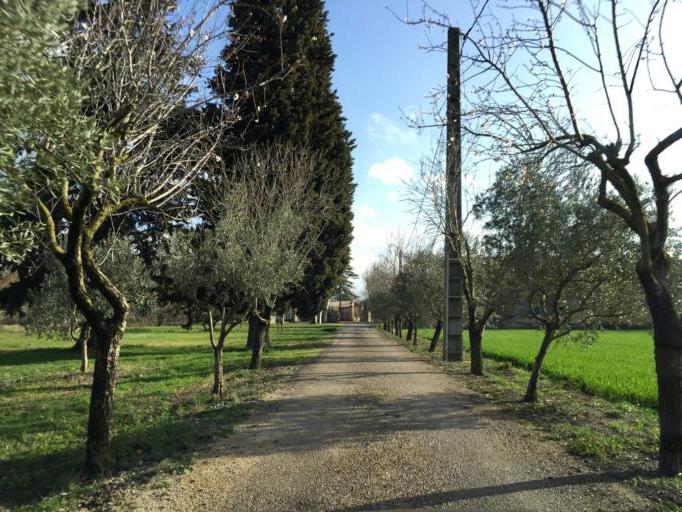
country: FR
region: Provence-Alpes-Cote d'Azur
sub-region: Departement du Vaucluse
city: Orange
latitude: 44.1389
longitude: 4.8327
